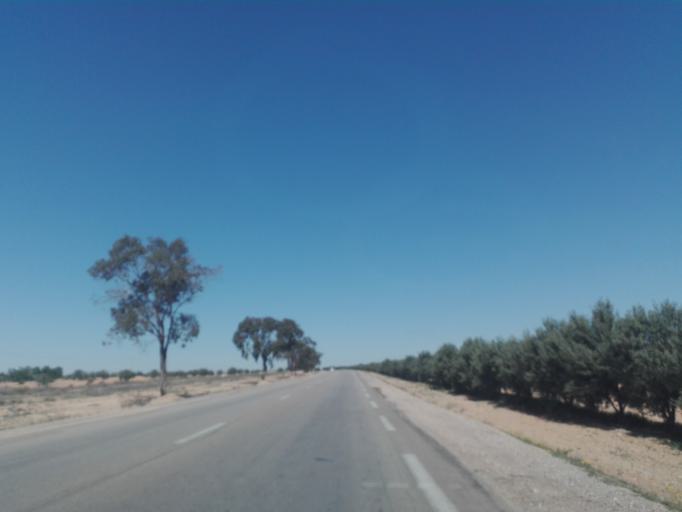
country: TN
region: Safaqis
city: Bi'r `Ali Bin Khalifah
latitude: 34.7495
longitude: 10.3496
